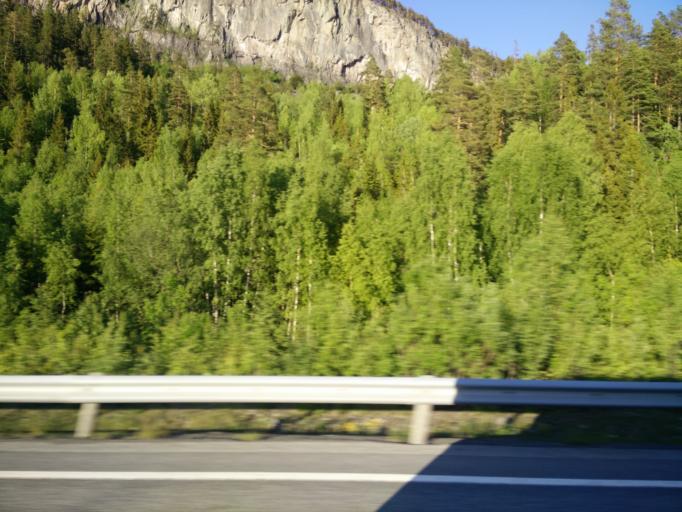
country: NO
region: Buskerud
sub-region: Hole
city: Vik
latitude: 60.0113
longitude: 10.2710
